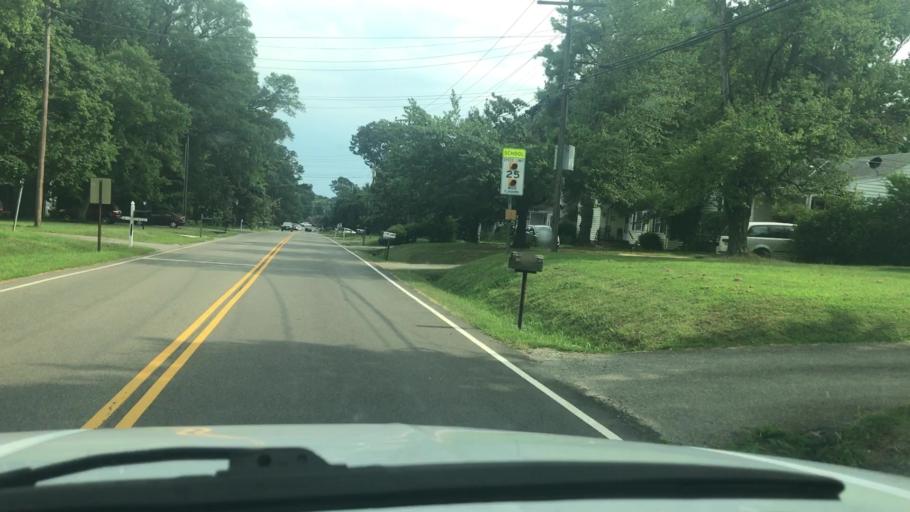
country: US
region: Virginia
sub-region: Henrico County
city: Laurel
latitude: 37.6326
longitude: -77.5449
